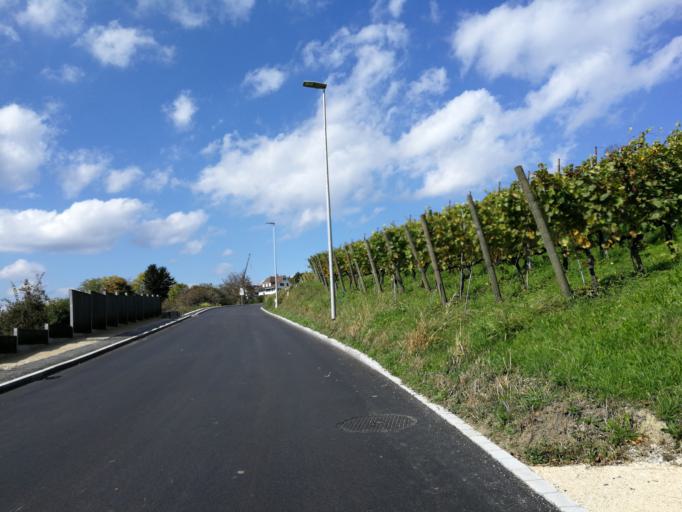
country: CH
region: Zurich
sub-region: Bezirk Meilen
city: Uetikon / Grossdorf
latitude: 47.2695
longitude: 8.6746
